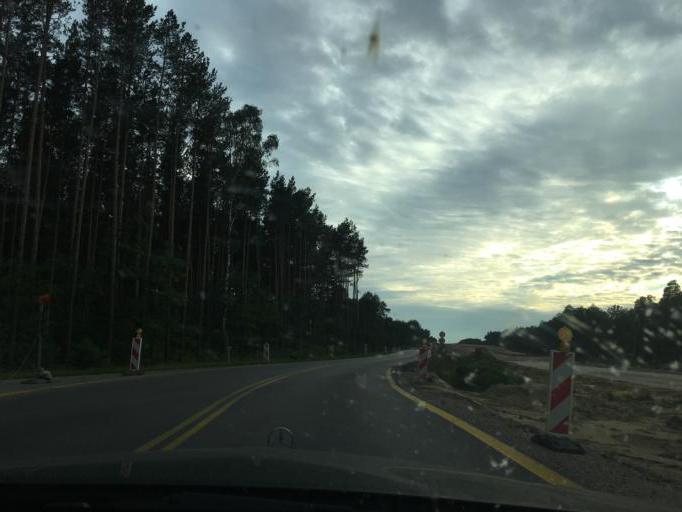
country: PL
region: Masovian Voivodeship
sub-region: Powiat ostrowski
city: Ostrow Mazowiecka
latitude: 52.7820
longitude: 21.8539
